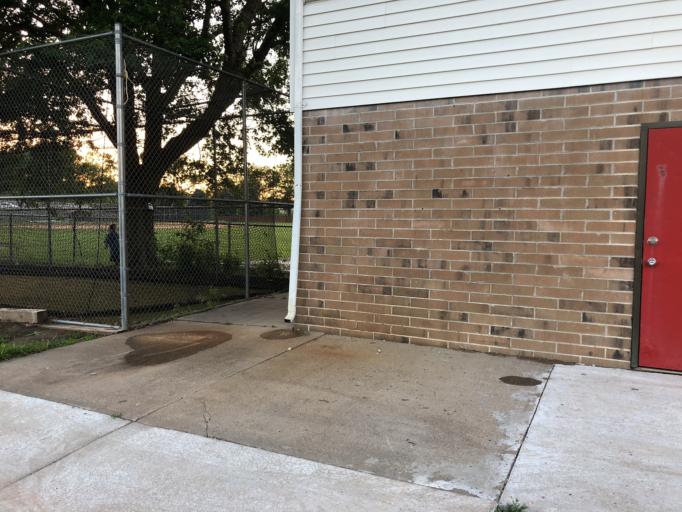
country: US
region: Nebraska
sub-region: Douglas County
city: Elkhorn
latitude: 41.2853
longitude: -96.2467
